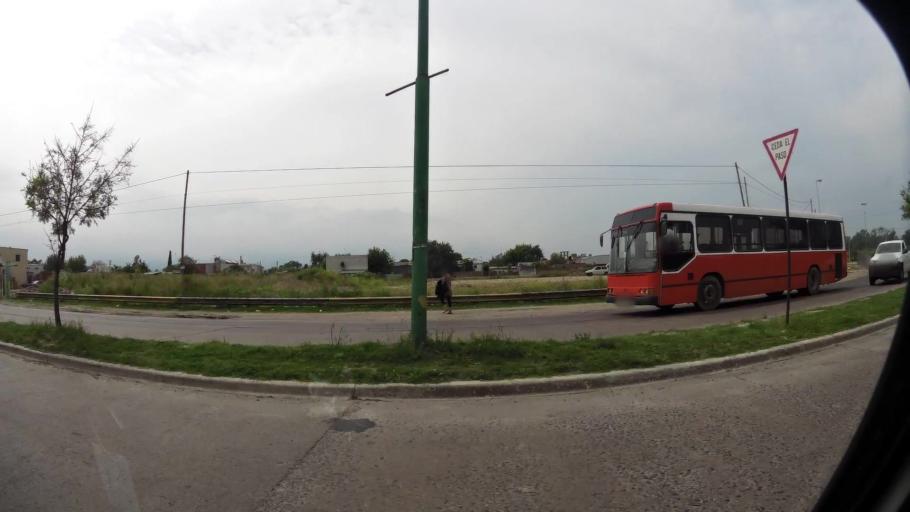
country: AR
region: Buenos Aires
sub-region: Partido de La Plata
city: La Plata
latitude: -34.9010
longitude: -57.9944
